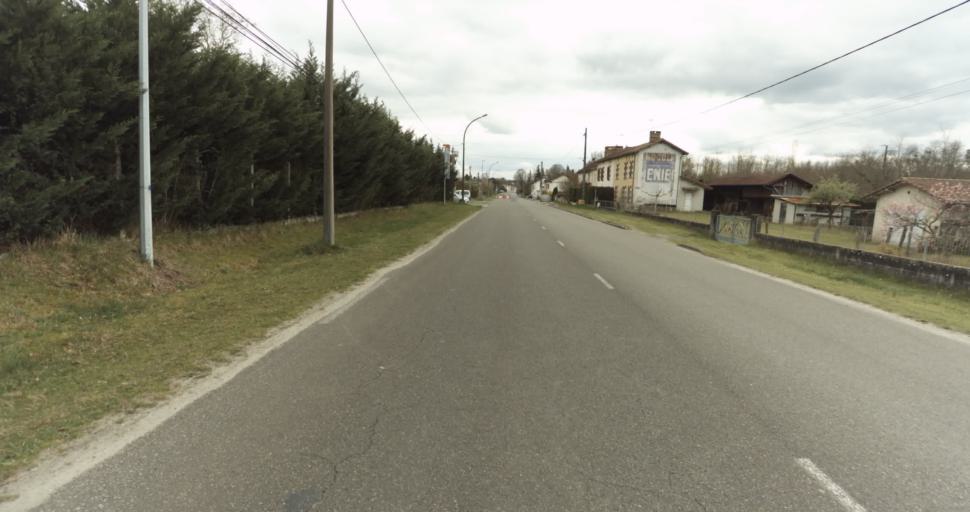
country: FR
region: Aquitaine
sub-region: Departement des Landes
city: Roquefort
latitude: 44.0425
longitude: -0.3221
